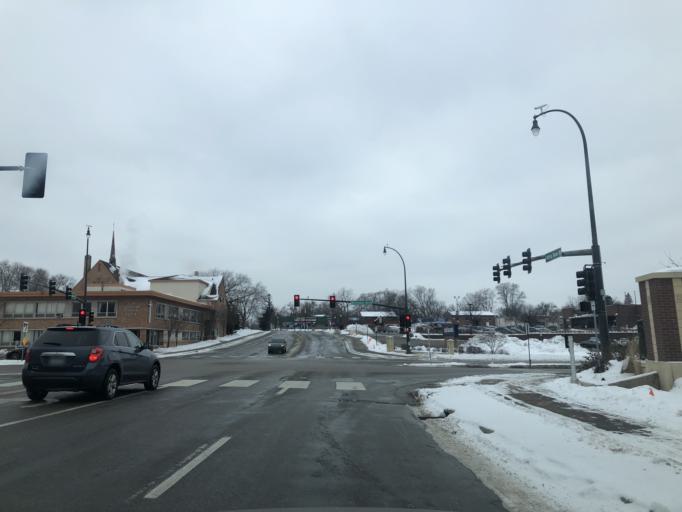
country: US
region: Minnesota
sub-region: Hennepin County
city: Robbinsdale
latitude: 45.0286
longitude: -93.3334
